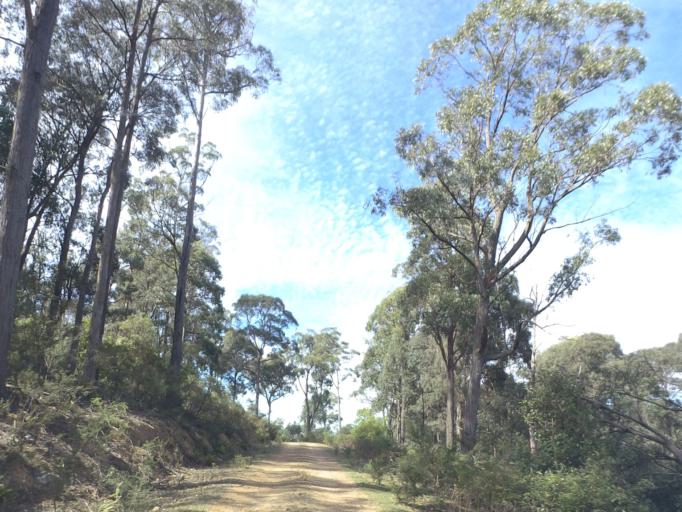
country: AU
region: Victoria
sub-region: Moorabool
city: Bacchus Marsh
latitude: -37.4359
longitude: 144.2530
